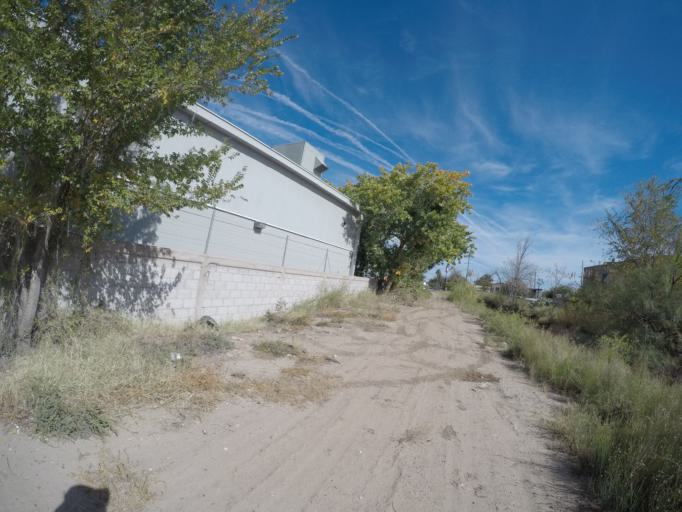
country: MX
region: Chihuahua
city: Ciudad Juarez
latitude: 31.7350
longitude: -106.4420
